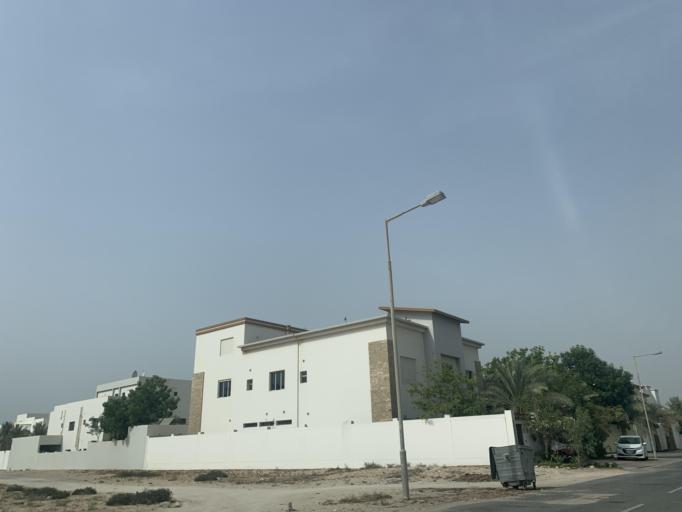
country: BH
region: Manama
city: Jidd Hafs
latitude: 26.2010
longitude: 50.4783
